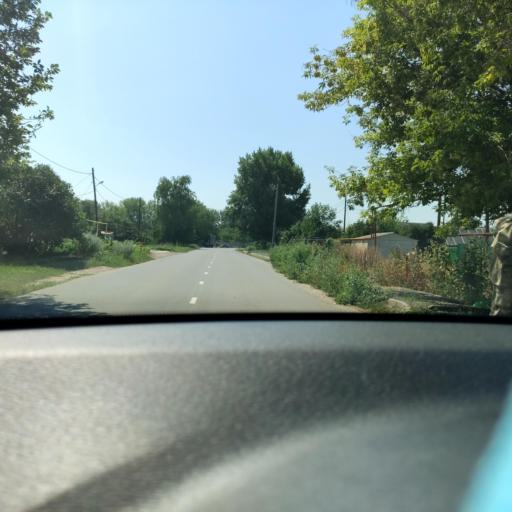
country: RU
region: Samara
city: Smyshlyayevka
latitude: 53.2171
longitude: 50.3328
